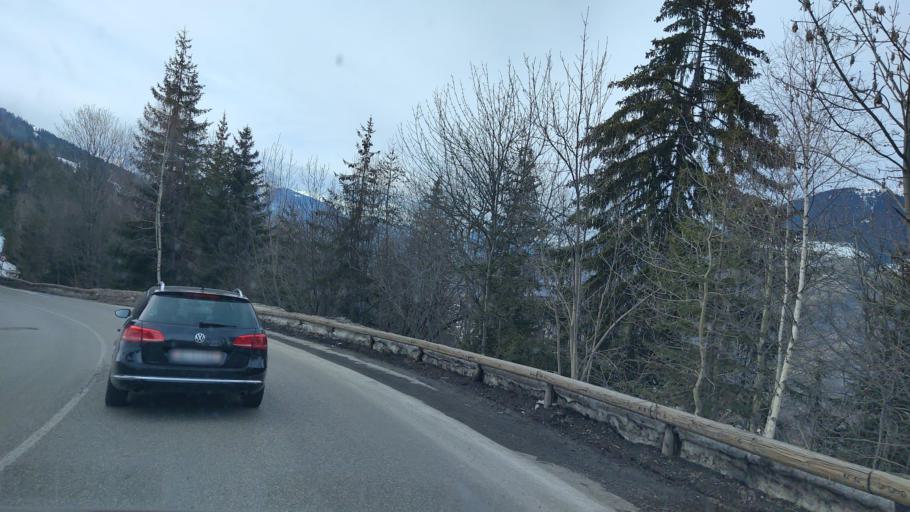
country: FR
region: Rhone-Alpes
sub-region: Departement de la Savoie
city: Saint-Bon-Tarentaise
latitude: 45.4290
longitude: 6.6322
